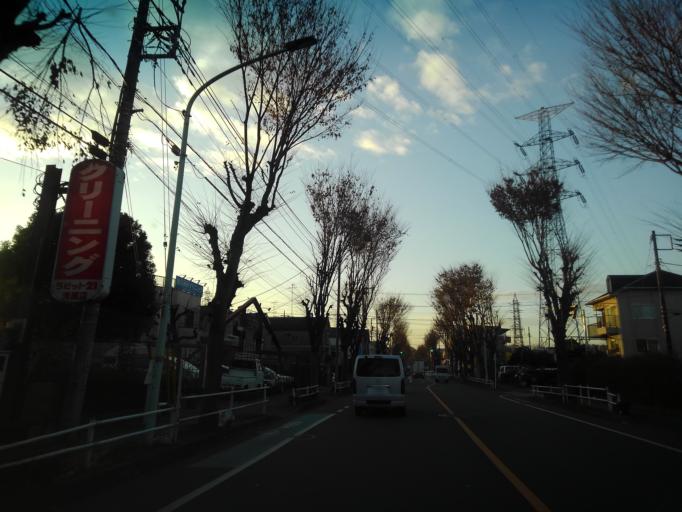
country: JP
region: Tokyo
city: Higashimurayama-shi
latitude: 35.7394
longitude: 139.4448
